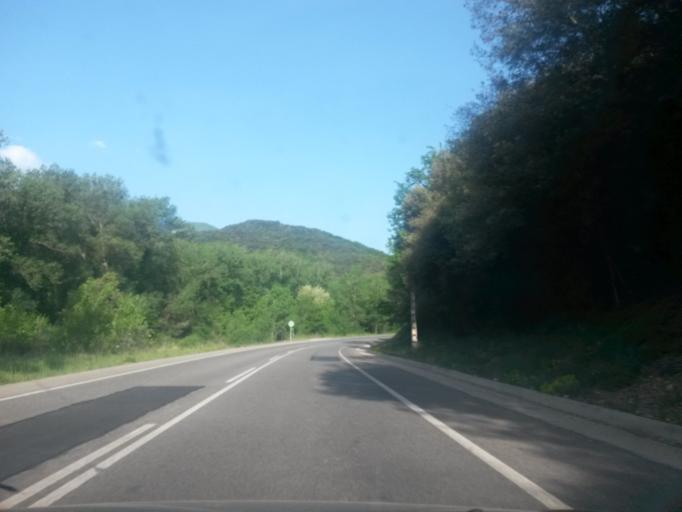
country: ES
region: Catalonia
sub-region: Provincia de Girona
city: les Planes d'Hostoles
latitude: 42.0399
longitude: 2.5680
